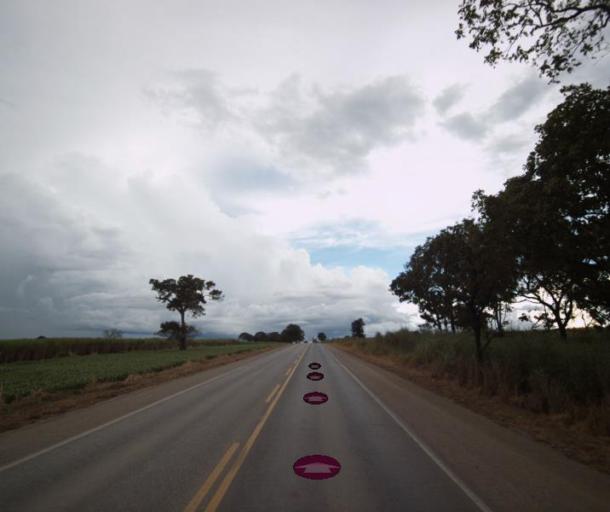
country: BR
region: Goias
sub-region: Itapaci
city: Itapaci
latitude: -14.8982
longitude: -49.3470
